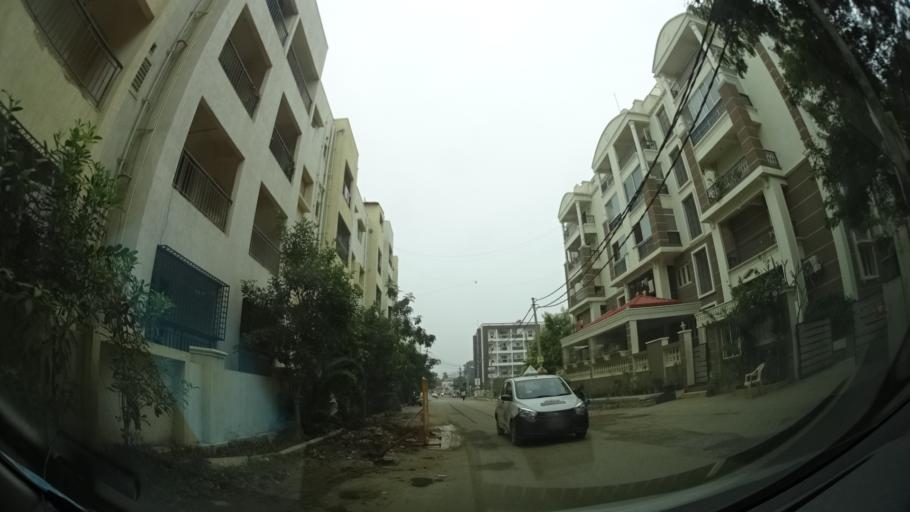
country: IN
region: Karnataka
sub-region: Bangalore Rural
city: Hoskote
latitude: 12.9684
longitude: 77.7397
